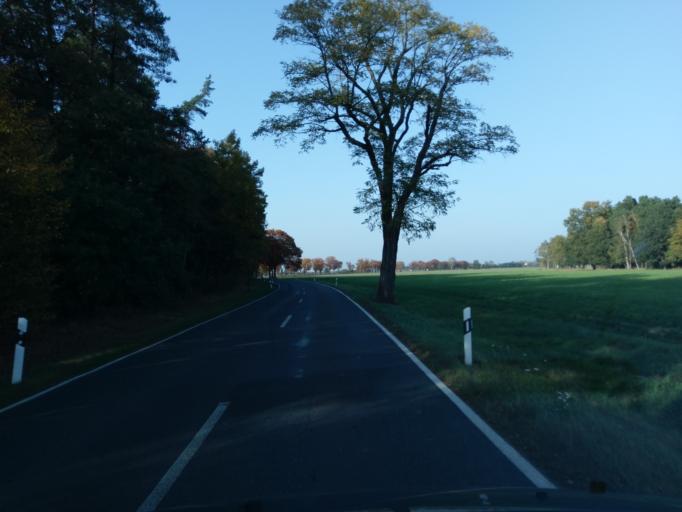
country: DE
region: Brandenburg
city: Falkenberg
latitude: 51.6206
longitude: 13.2316
